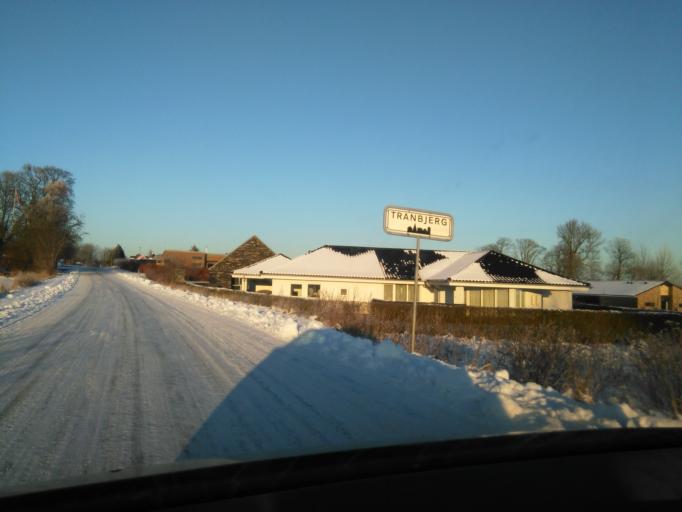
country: DK
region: Central Jutland
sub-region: Arhus Kommune
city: Tranbjerg
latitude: 56.0805
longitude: 10.1204
